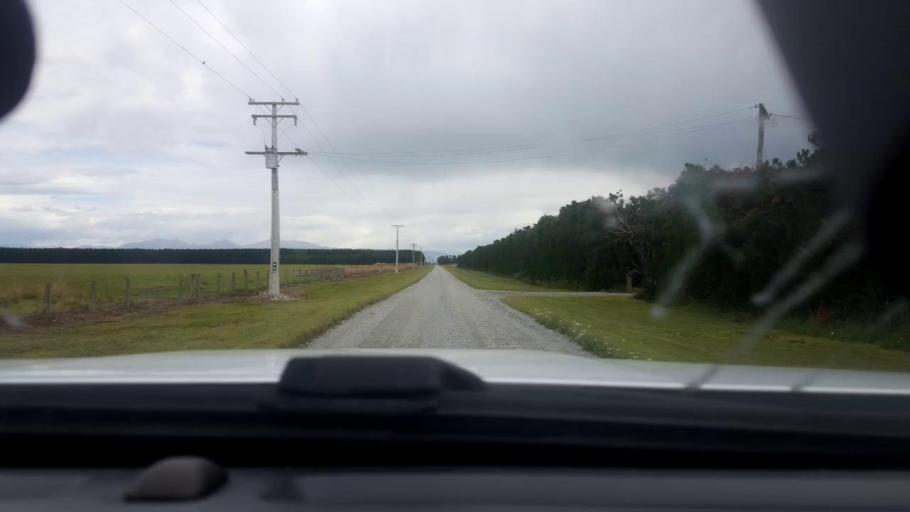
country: NZ
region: Canterbury
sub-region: Timaru District
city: Timaru
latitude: -44.1674
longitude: 171.4113
